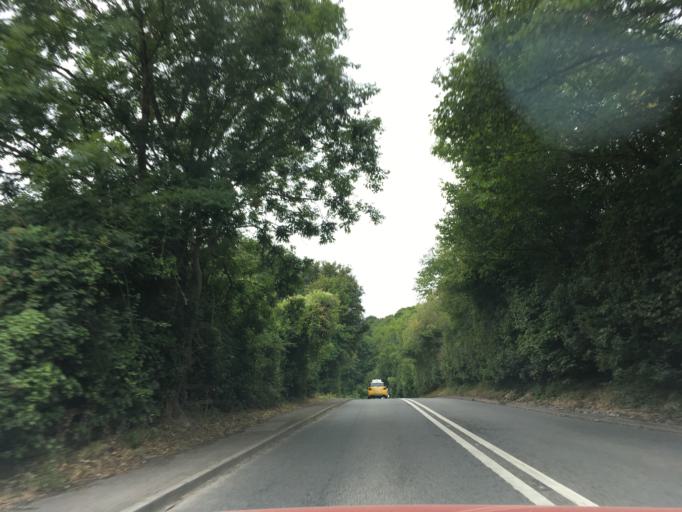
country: GB
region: Wales
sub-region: Monmouthshire
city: Gilwern
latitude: 51.8346
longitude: -3.0669
